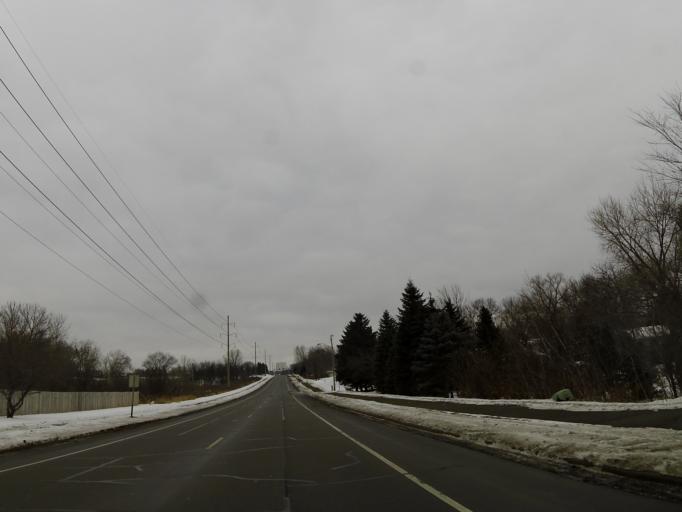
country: US
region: Minnesota
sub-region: Dakota County
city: Burnsville
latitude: 44.7456
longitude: -93.2583
